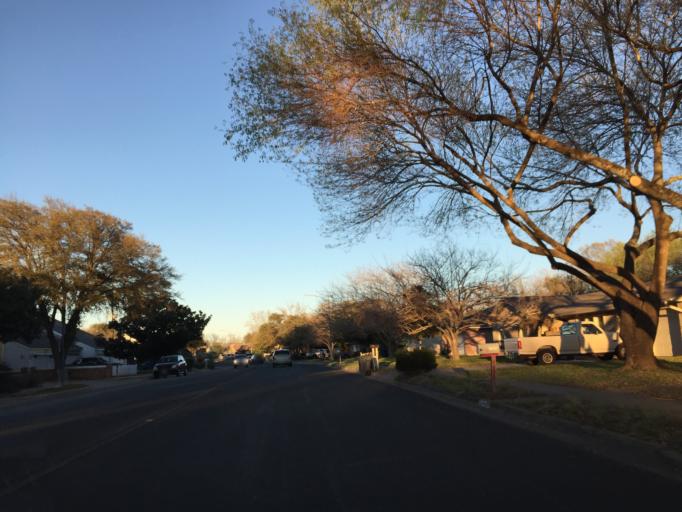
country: US
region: Texas
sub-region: Williamson County
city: Jollyville
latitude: 30.4313
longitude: -97.7712
